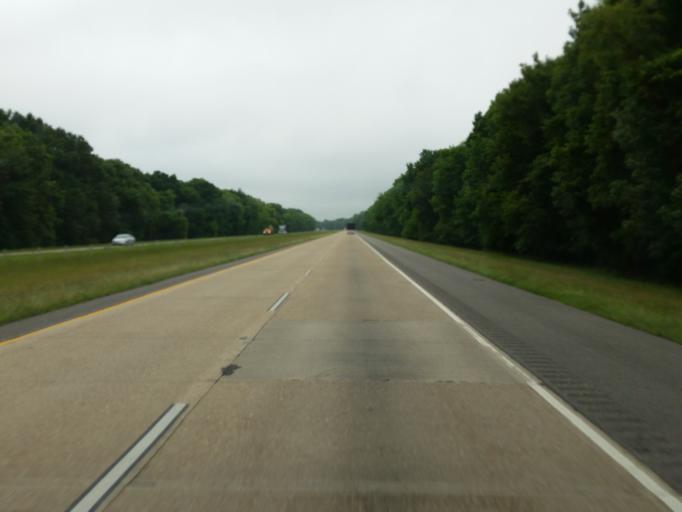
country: US
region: Louisiana
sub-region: Madison Parish
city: Tallulah
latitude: 32.3427
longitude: -91.0753
